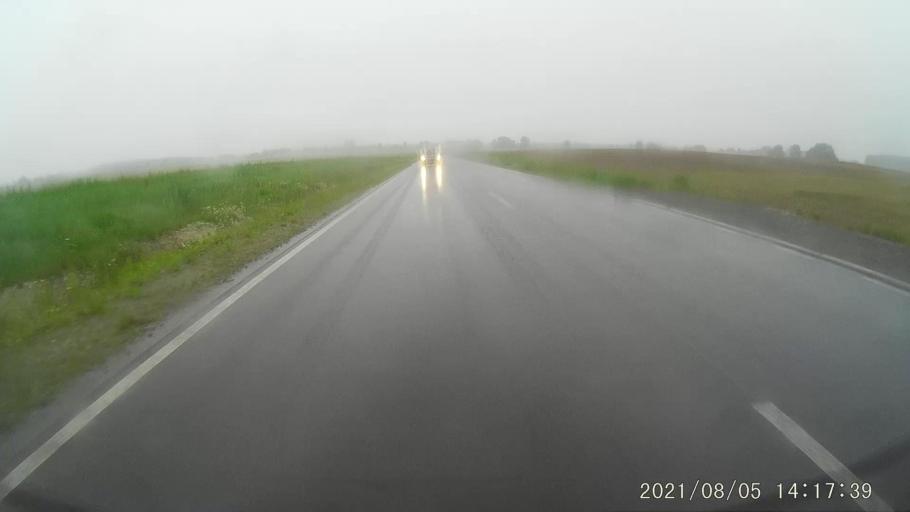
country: PL
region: Opole Voivodeship
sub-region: Powiat prudnicki
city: Biala
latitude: 50.4622
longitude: 17.7023
